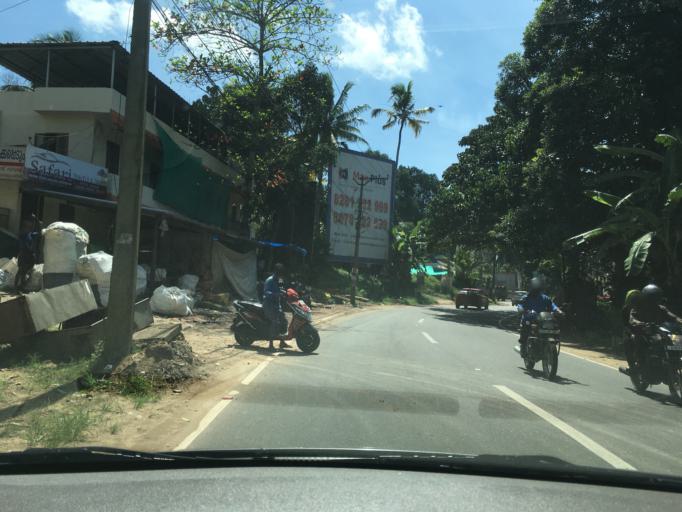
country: IN
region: Kerala
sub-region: Thiruvananthapuram
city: Nedumangad
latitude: 8.5734
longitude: 76.9961
